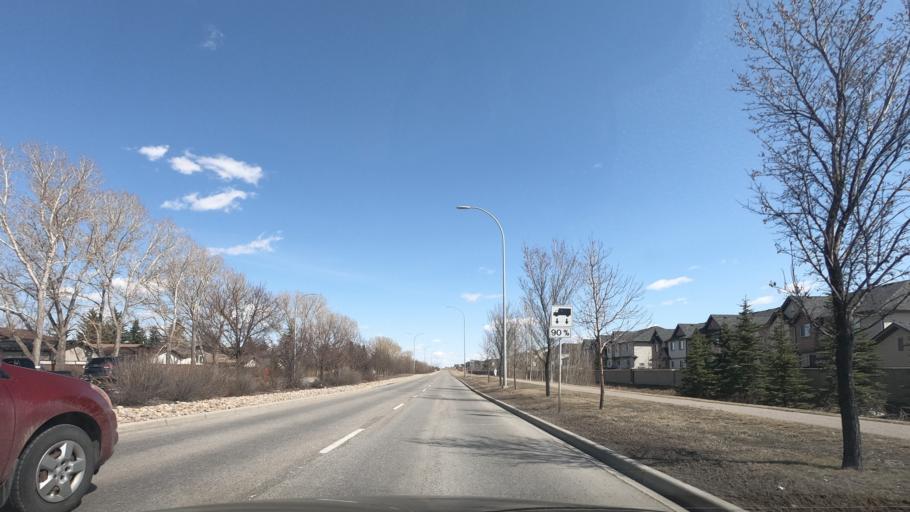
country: CA
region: Alberta
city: Airdrie
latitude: 51.2707
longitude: -113.9891
